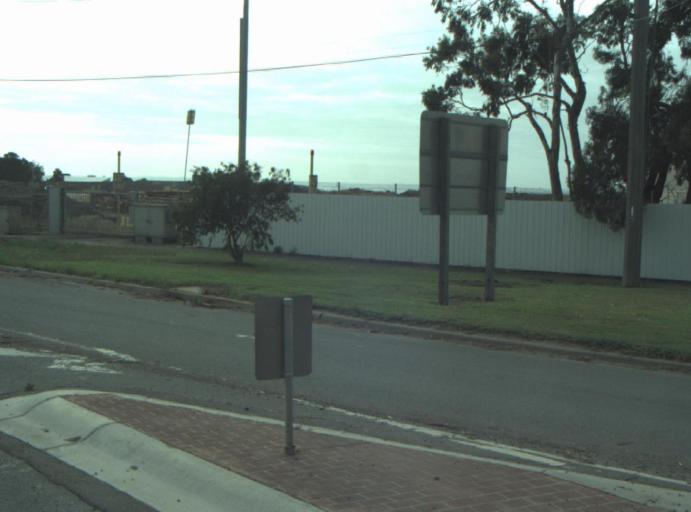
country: AU
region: Victoria
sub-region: Greater Geelong
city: Bell Park
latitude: -38.1001
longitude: 144.3658
